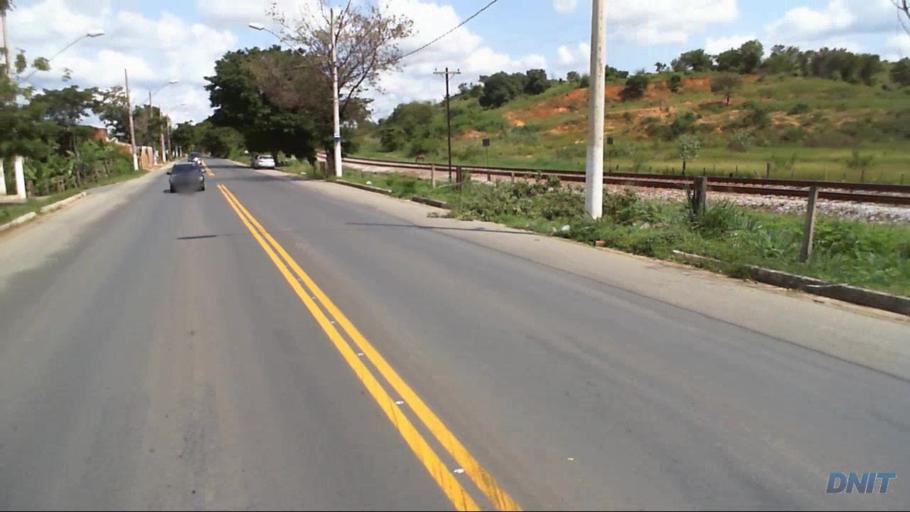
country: BR
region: Minas Gerais
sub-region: Governador Valadares
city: Governador Valadares
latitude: -18.9115
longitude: -41.9961
